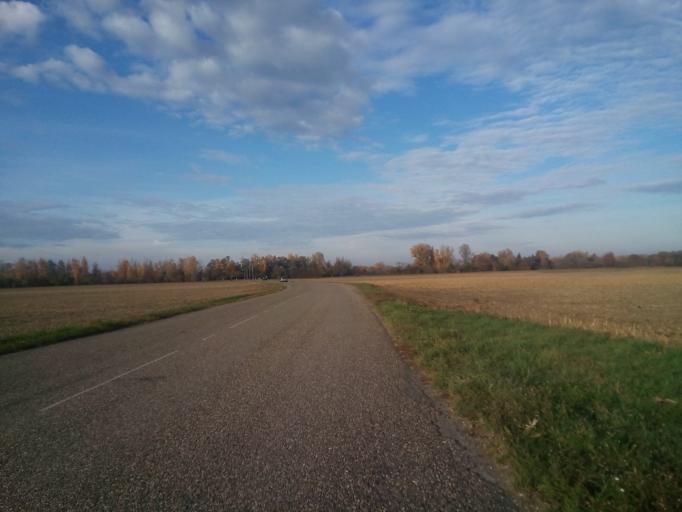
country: FR
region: Alsace
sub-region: Departement du Bas-Rhin
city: Herrlisheim
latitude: 48.6988
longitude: 7.9210
